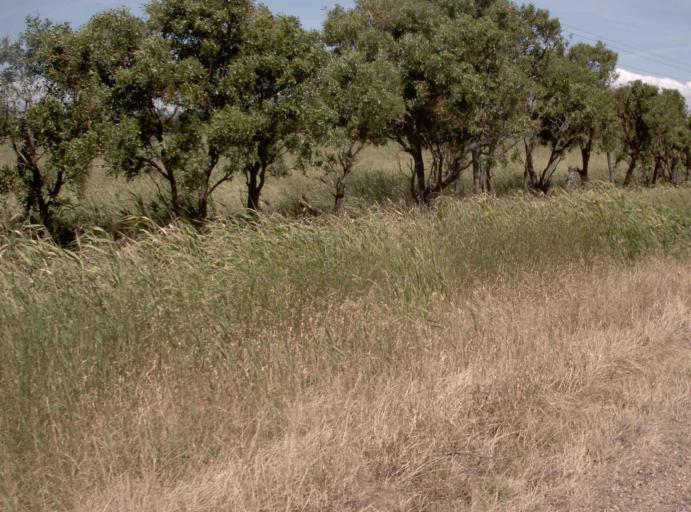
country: AU
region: Victoria
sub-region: Wellington
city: Heyfield
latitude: -38.0027
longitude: 146.8839
